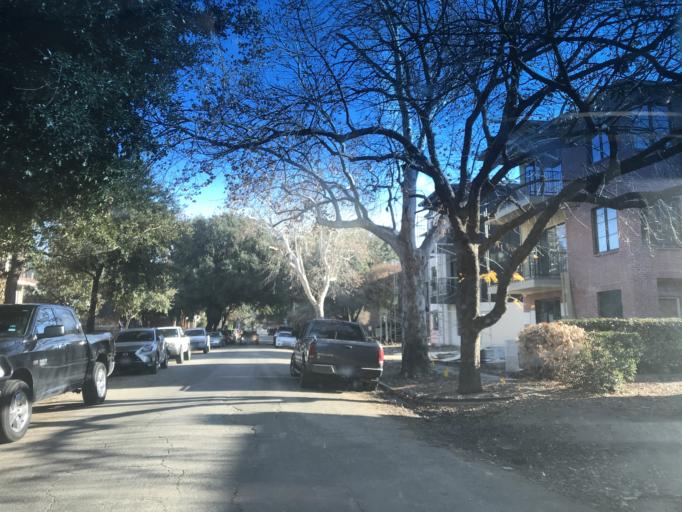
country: US
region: Texas
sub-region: Dallas County
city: Highland Park
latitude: 32.8183
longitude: -96.8093
